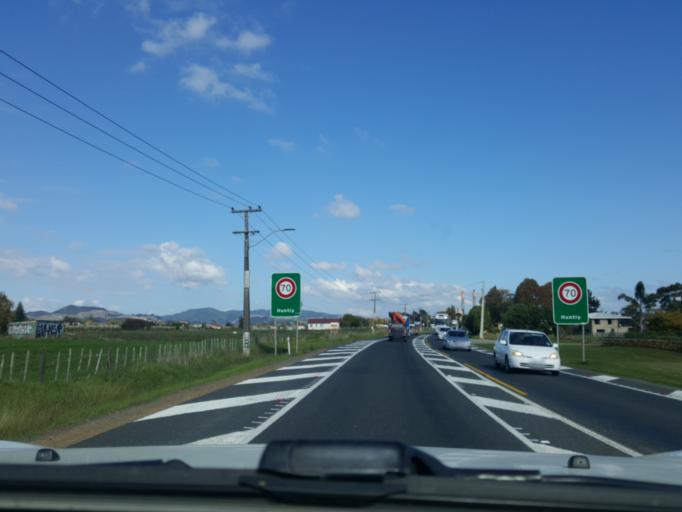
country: NZ
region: Waikato
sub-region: Waikato District
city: Te Kauwhata
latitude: -37.5199
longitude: 175.1626
